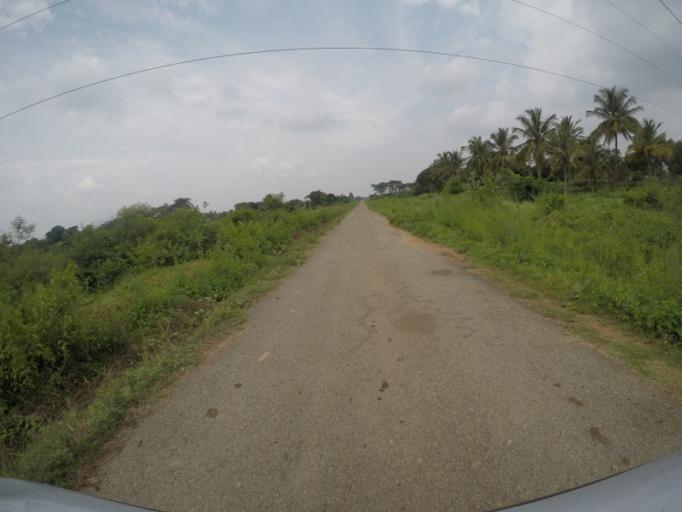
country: IN
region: Karnataka
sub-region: Mandya
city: Malavalli
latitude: 12.4132
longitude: 77.2079
